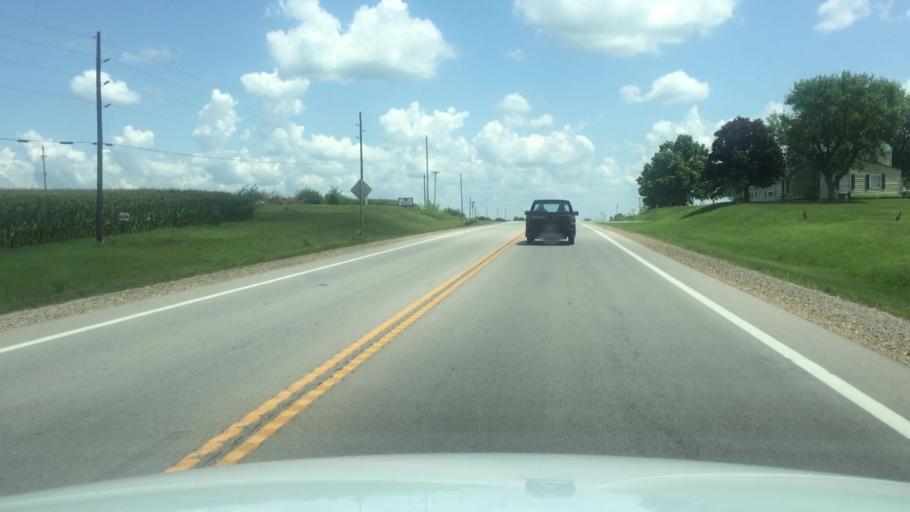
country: US
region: Kansas
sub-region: Brown County
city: Horton
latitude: 39.6673
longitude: -95.5099
